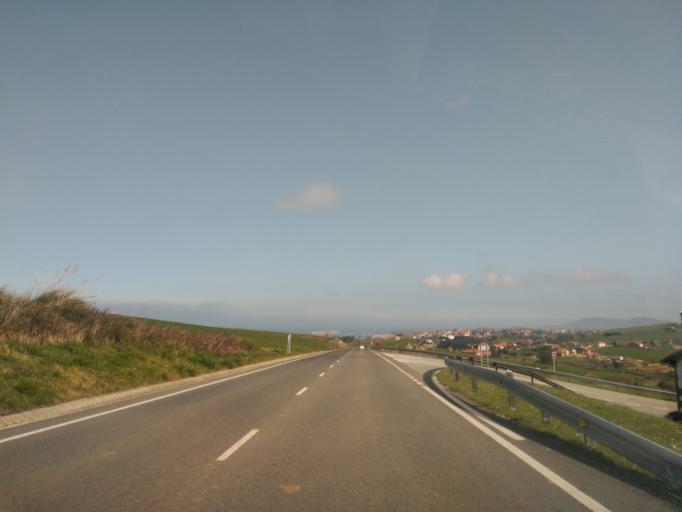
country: ES
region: Cantabria
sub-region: Provincia de Cantabria
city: Santillana
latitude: 43.4120
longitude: -4.0780
